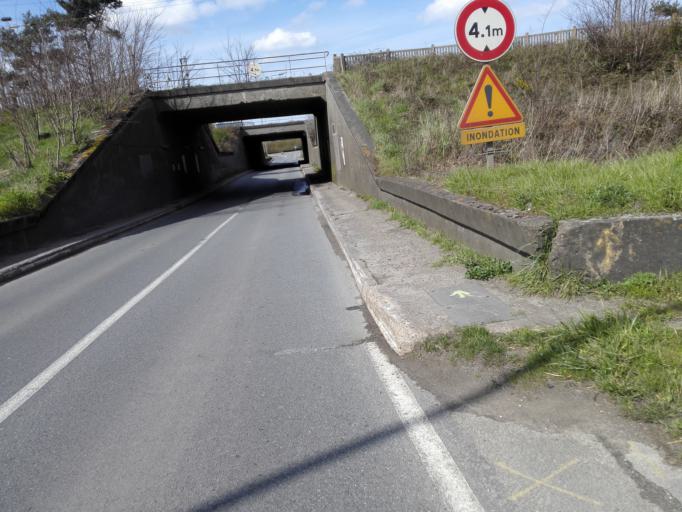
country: FR
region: Nord-Pas-de-Calais
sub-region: Departement du Nord
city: Grande-Synthe
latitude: 50.9966
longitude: 2.2933
